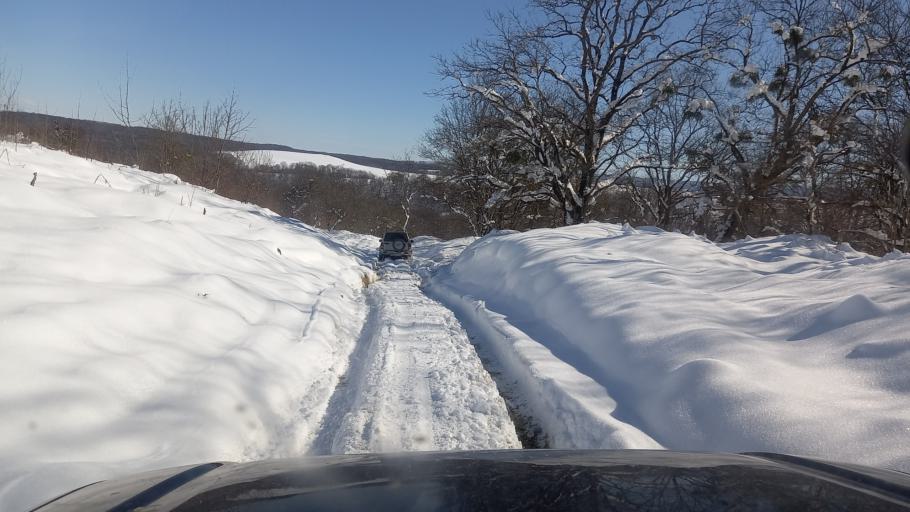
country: RU
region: Krasnodarskiy
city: Gubskaya
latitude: 44.3374
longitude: 40.4453
